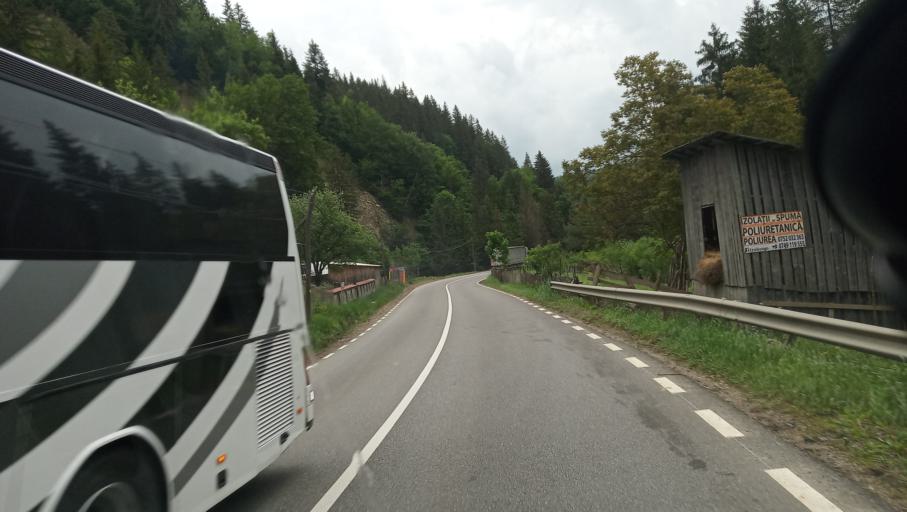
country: RO
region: Neamt
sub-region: Comuna Pipirig
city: Dolhesti
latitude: 47.1956
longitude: 26.0465
